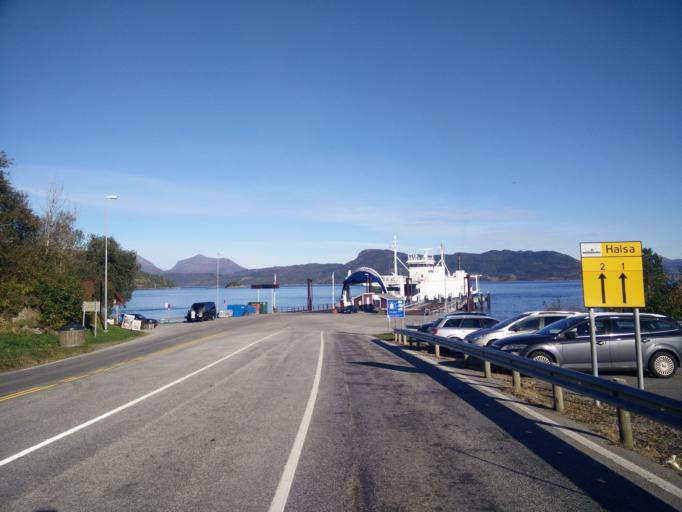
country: NO
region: More og Romsdal
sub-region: Tingvoll
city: Tingvoll
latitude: 63.0525
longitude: 8.1237
